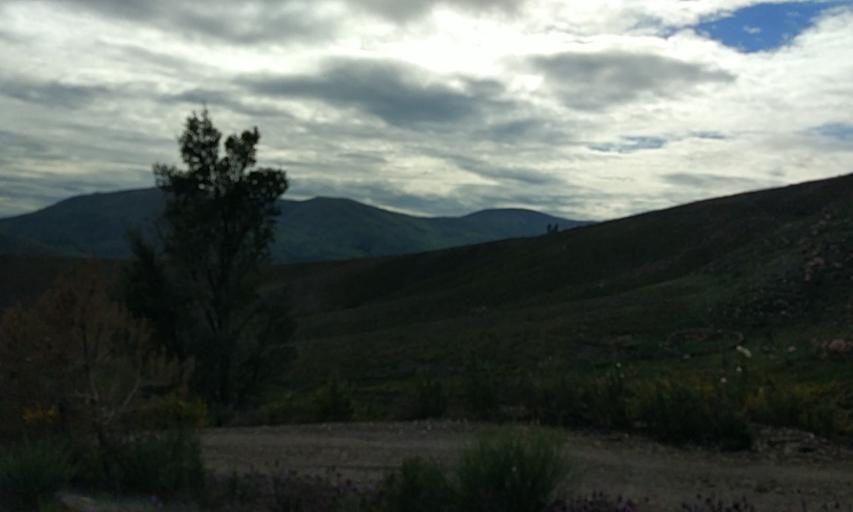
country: ES
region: Extremadura
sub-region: Provincia de Caceres
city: Acebo
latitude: 40.2125
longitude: -6.6760
